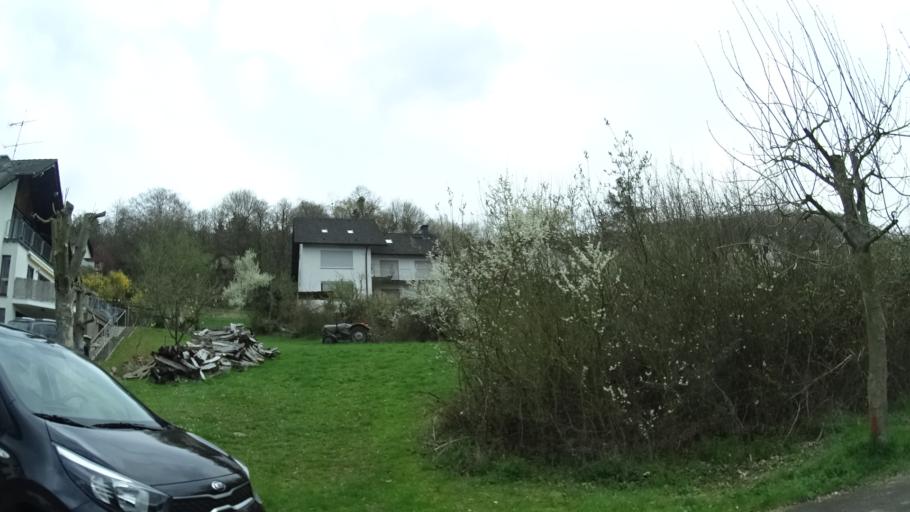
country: DE
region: Rheinland-Pfalz
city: Kirn
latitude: 49.7982
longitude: 7.4644
